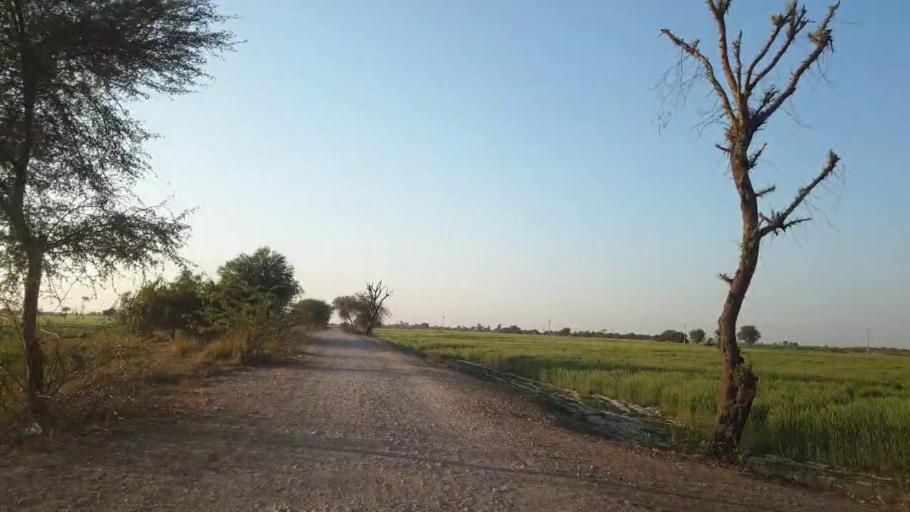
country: PK
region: Sindh
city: Mirpur Khas
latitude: 25.6946
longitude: 69.0505
